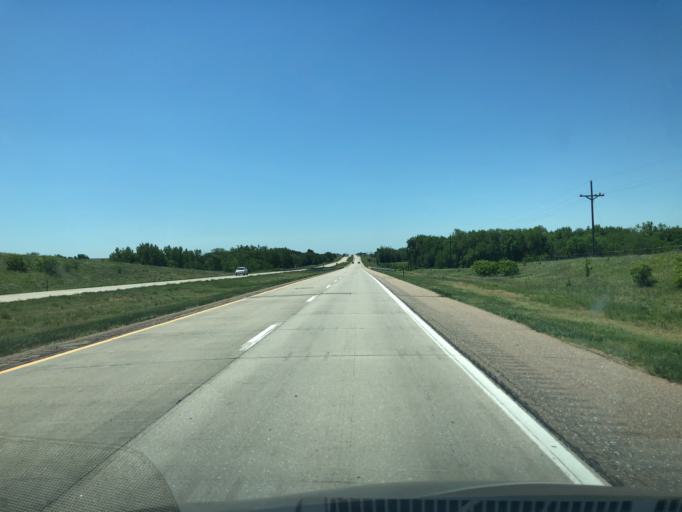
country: US
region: Nebraska
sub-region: Thayer County
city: Hebron
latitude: 40.2303
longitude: -97.5768
